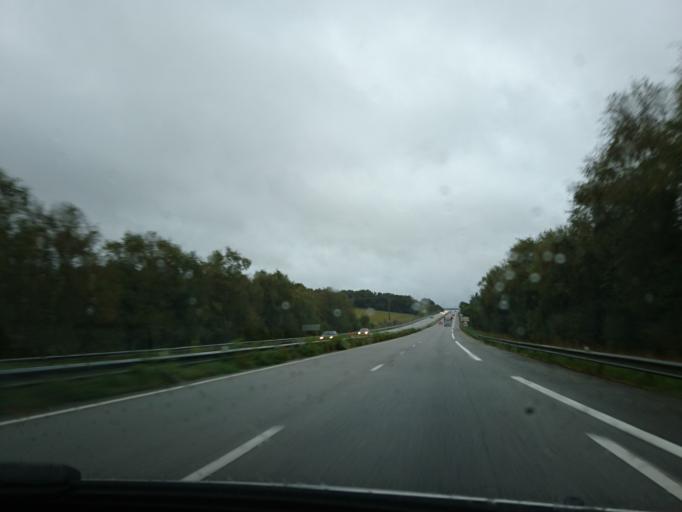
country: FR
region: Brittany
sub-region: Departement du Finistere
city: Chateaulin
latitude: 48.2239
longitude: -4.0714
